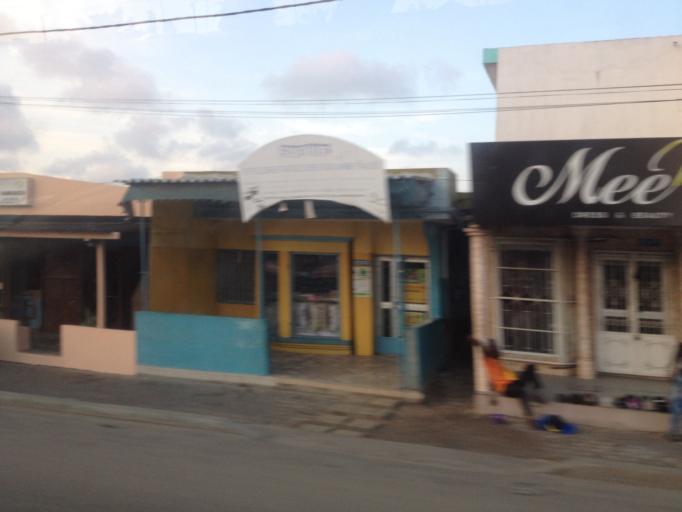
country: BJ
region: Littoral
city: Cotonou
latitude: 6.3700
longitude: 2.4532
